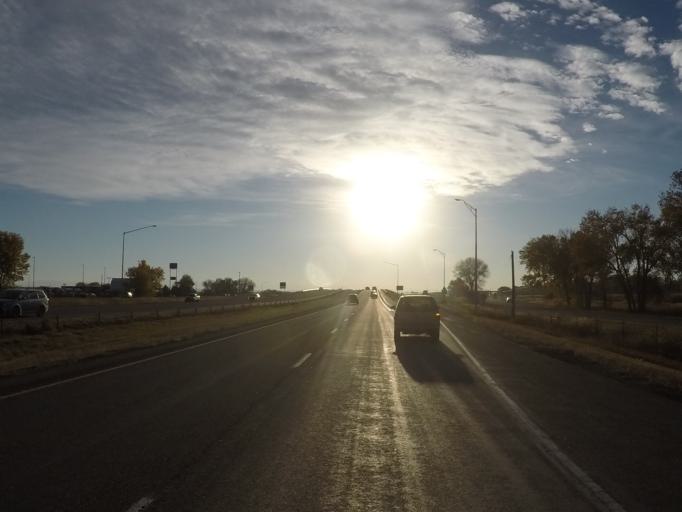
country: US
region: Montana
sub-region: Yellowstone County
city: Laurel
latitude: 45.6854
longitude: -108.7006
